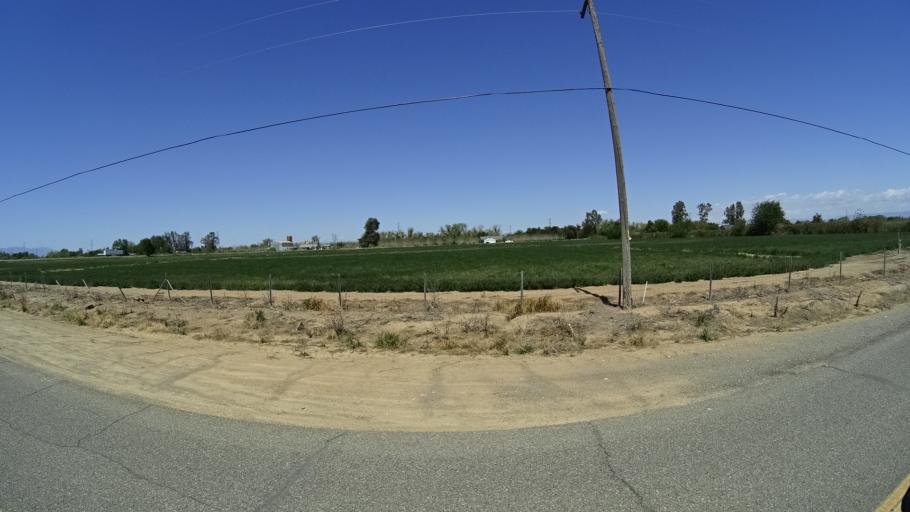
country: US
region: California
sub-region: Glenn County
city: Orland
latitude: 39.7943
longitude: -122.1990
